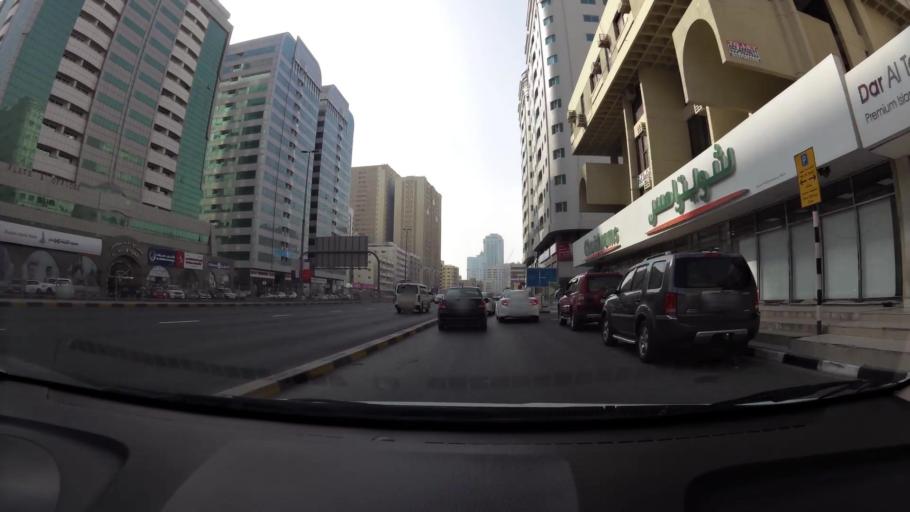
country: AE
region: Ash Shariqah
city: Sharjah
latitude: 25.3351
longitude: 55.3914
